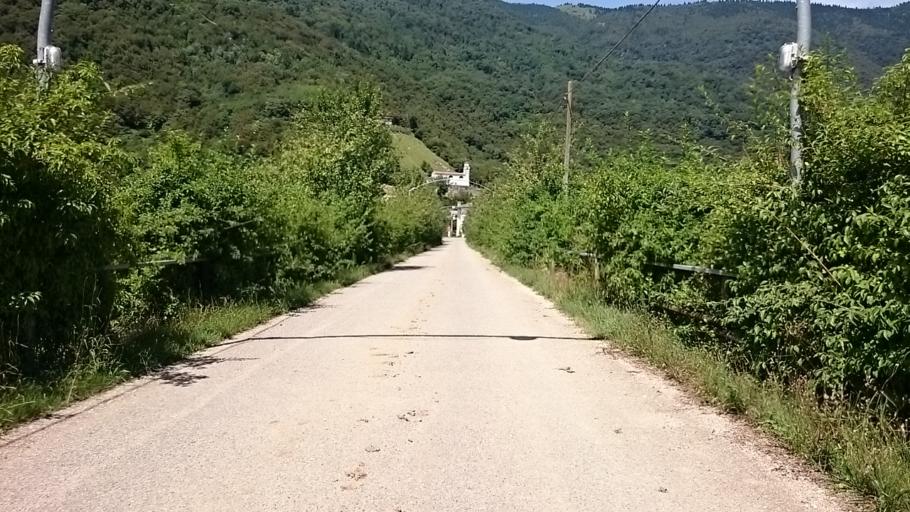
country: IT
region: Veneto
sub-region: Provincia di Treviso
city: Tarzo
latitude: 45.9770
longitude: 12.1951
